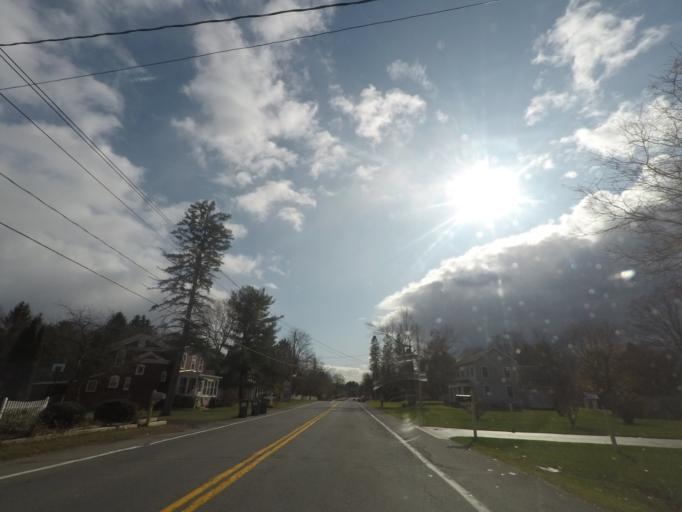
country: US
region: New York
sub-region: Saratoga County
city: Country Knolls
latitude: 42.9049
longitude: -73.8210
